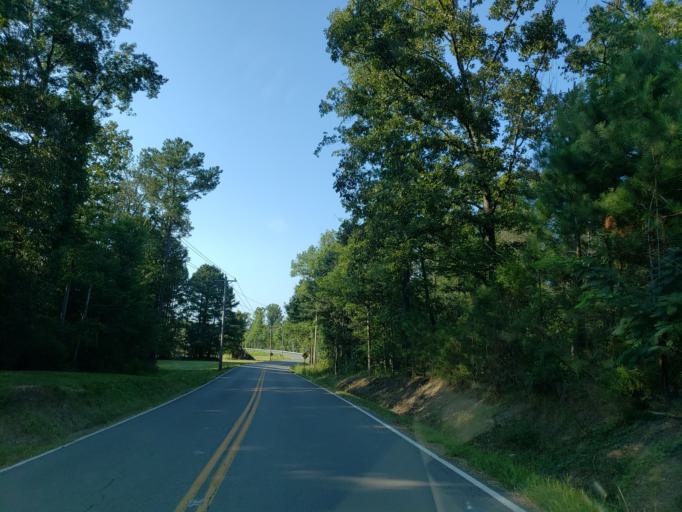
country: US
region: Tennessee
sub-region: Bradley County
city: Wildwood Lake
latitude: 35.0441
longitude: -84.7455
